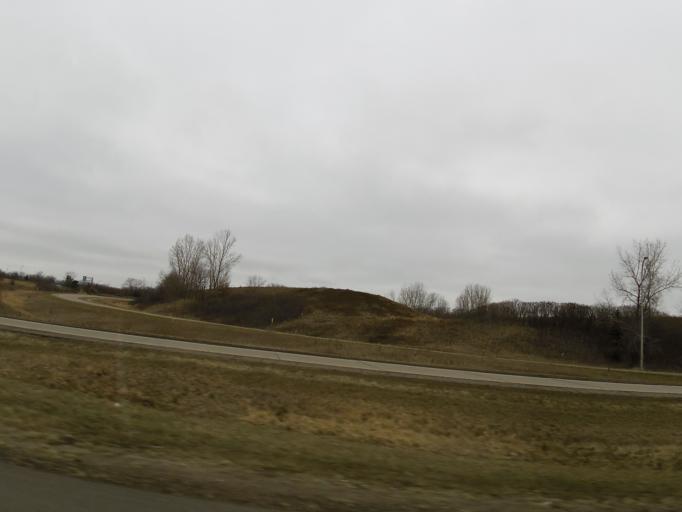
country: US
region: Minnesota
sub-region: Dakota County
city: Apple Valley
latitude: 44.7806
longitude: -93.2138
